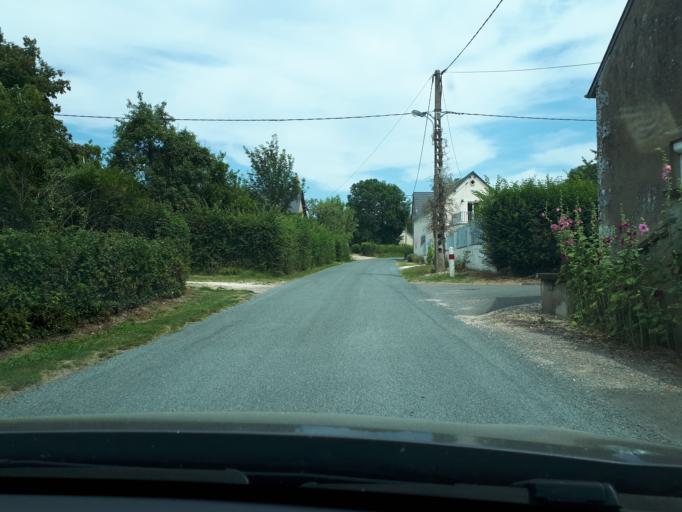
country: FR
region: Centre
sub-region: Departement du Cher
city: Sancerre
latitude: 47.2866
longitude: 2.7540
